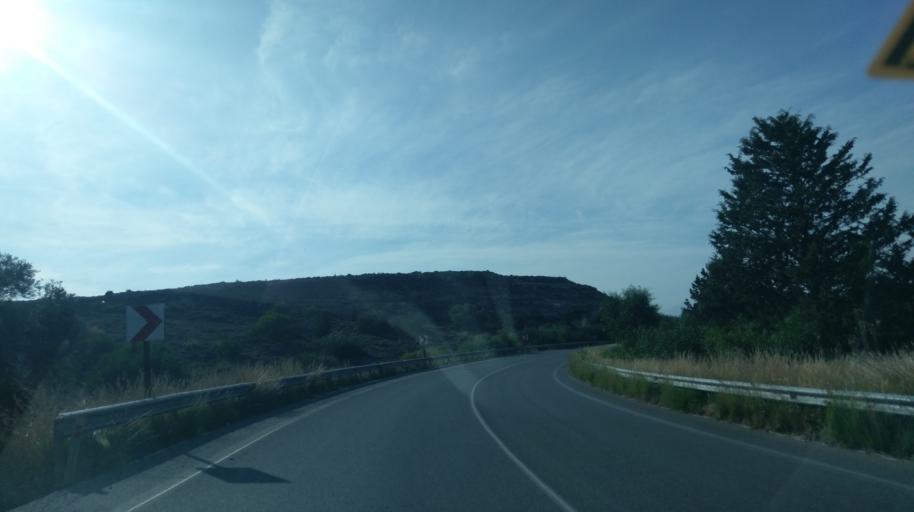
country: CY
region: Ammochostos
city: Trikomo
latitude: 35.2790
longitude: 33.8451
